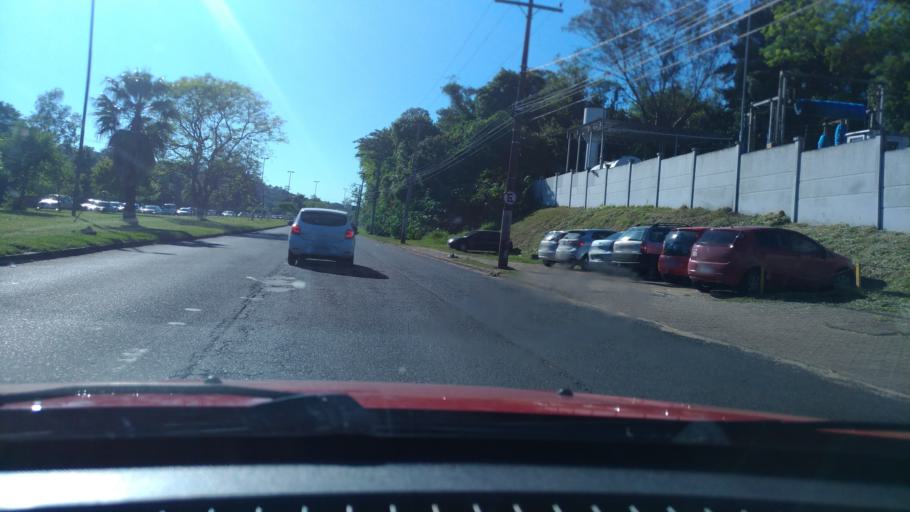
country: BR
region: Rio Grande do Sul
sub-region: Viamao
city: Viamao
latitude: -30.0771
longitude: -51.1225
